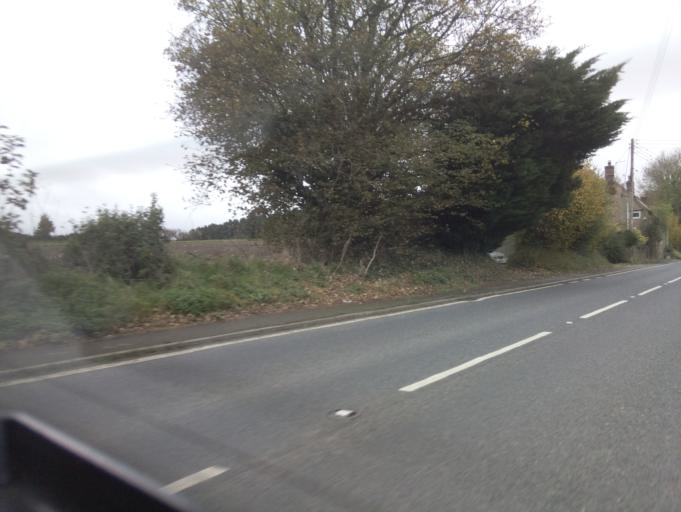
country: GB
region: England
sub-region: Somerset
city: South Petherton
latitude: 50.9382
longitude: -2.8110
